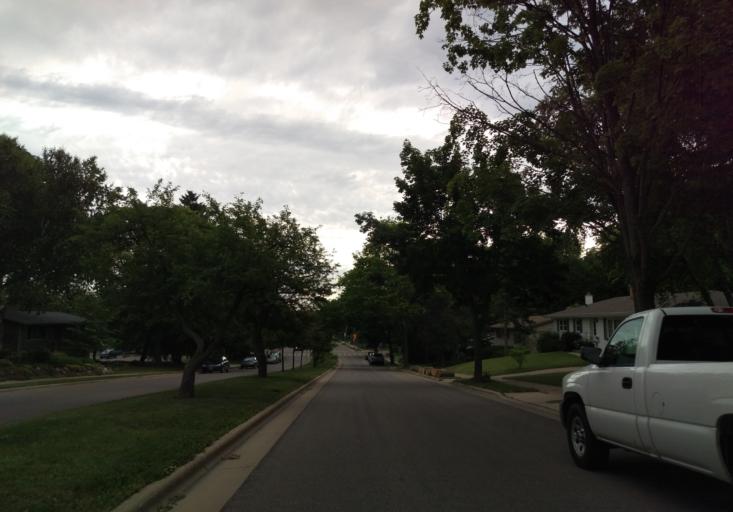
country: US
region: Wisconsin
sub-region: Dane County
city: Shorewood Hills
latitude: 43.0685
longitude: -89.4650
